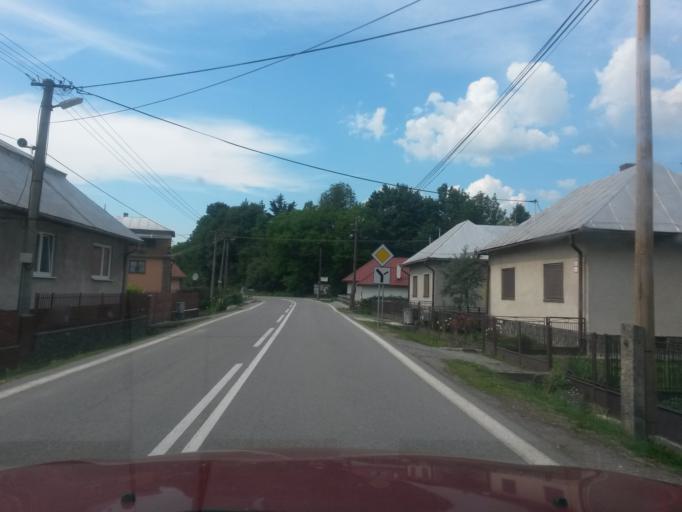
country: SK
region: Presovsky
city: Snina
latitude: 48.9957
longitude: 22.2356
